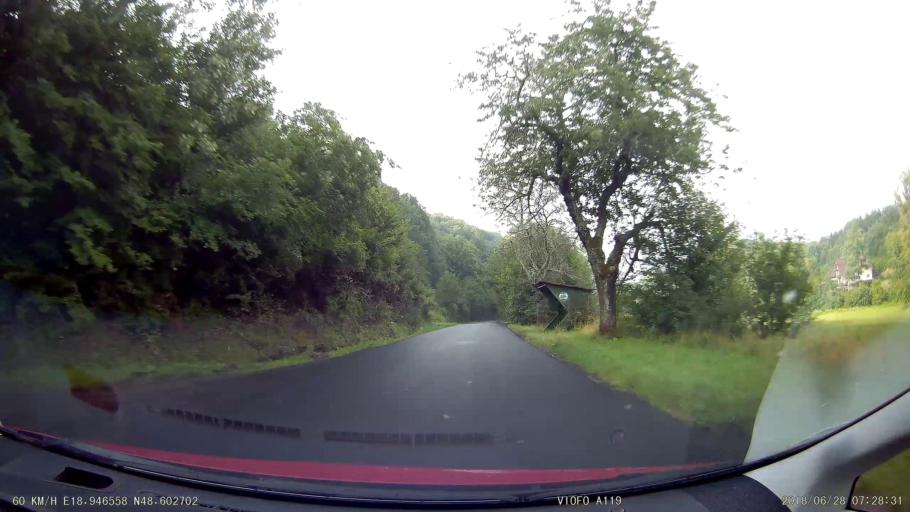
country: SK
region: Banskobystricky
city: Ziar nad Hronom
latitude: 48.6026
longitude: 18.9466
